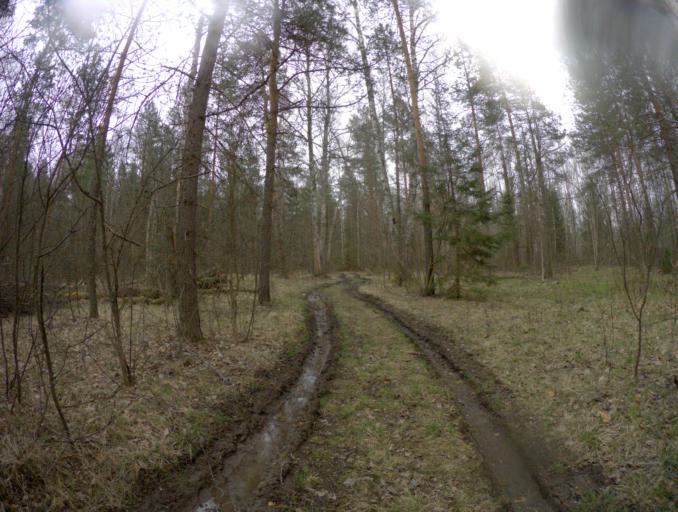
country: RU
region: Vladimir
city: Sudogda
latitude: 56.0281
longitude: 40.7935
